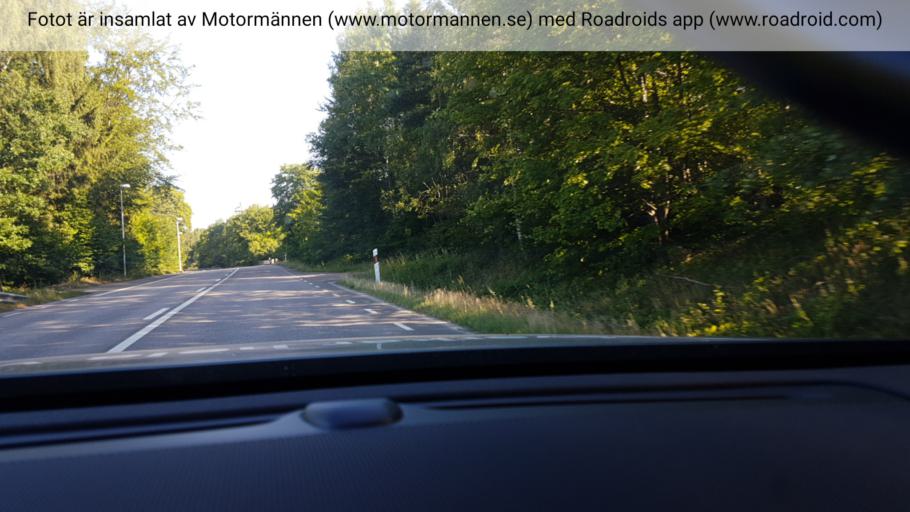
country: SE
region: Skane
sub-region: Hassleholms Kommun
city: Bjarnum
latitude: 56.3251
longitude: 13.6820
